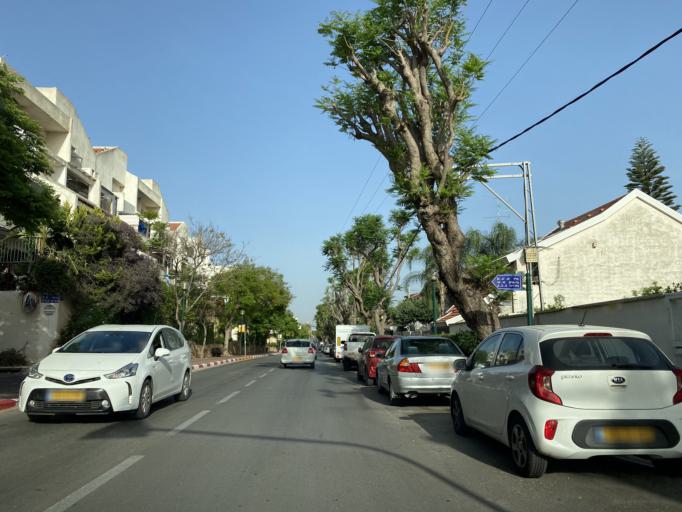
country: IL
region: Central District
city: Kfar Saba
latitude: 32.1829
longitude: 34.9138
